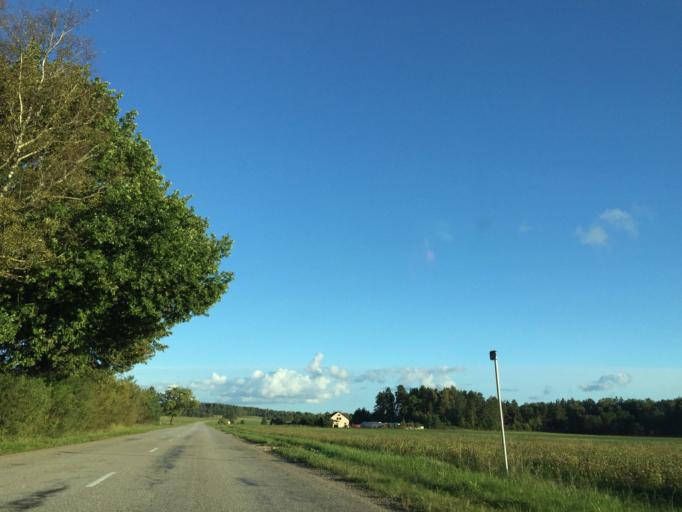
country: LV
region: Kuldigas Rajons
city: Kuldiga
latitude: 56.9322
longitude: 22.0388
